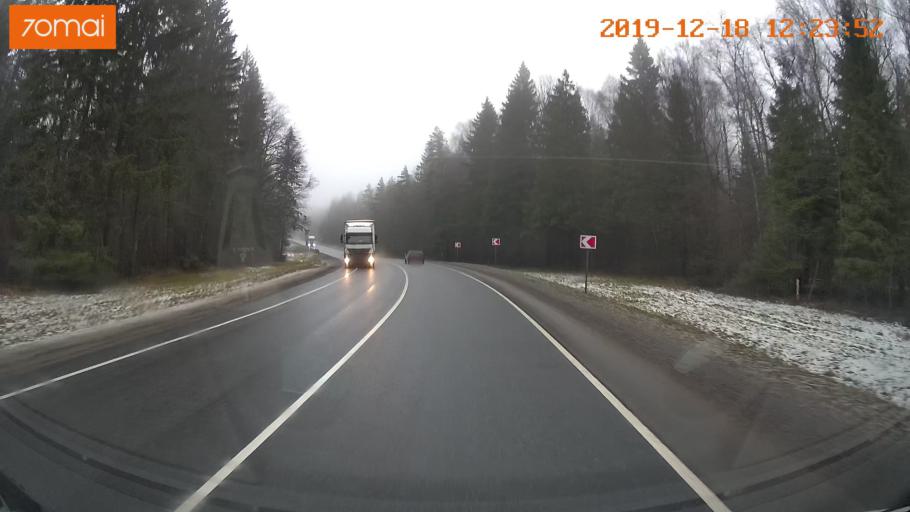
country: RU
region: Moskovskaya
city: Novopetrovskoye
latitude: 56.0176
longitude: 36.4982
